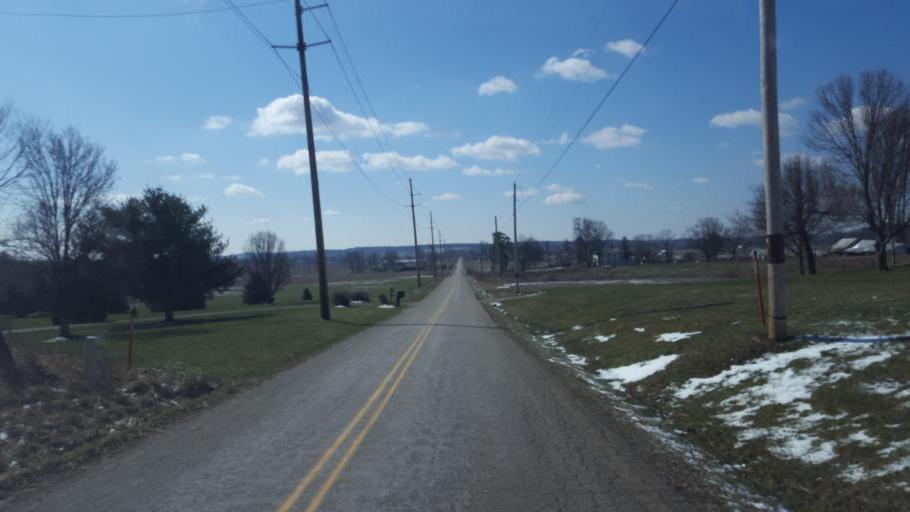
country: US
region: Ohio
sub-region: Licking County
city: Utica
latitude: 40.2850
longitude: -82.4745
